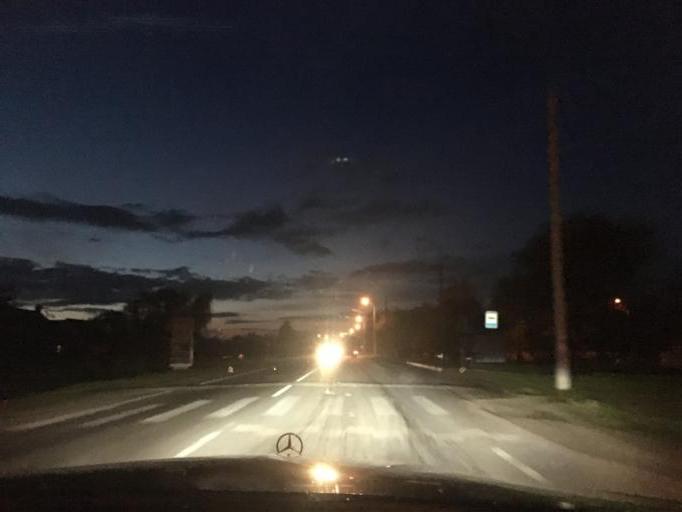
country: BY
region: Brest
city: Brest
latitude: 52.0655
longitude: 23.6867
